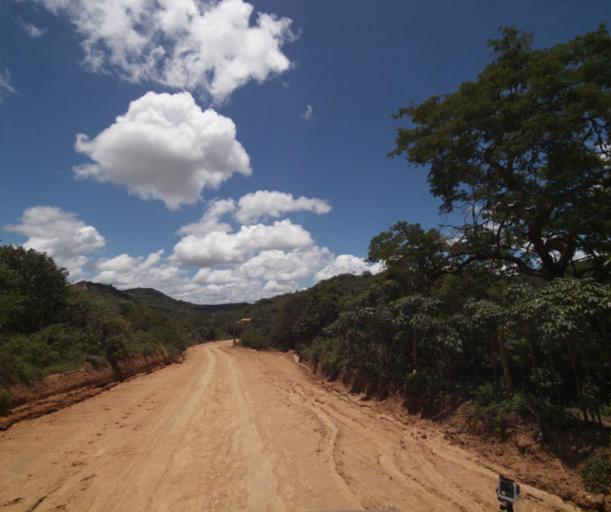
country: BR
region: Bahia
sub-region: Pocoes
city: Pocoes
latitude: -14.3840
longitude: -40.4173
